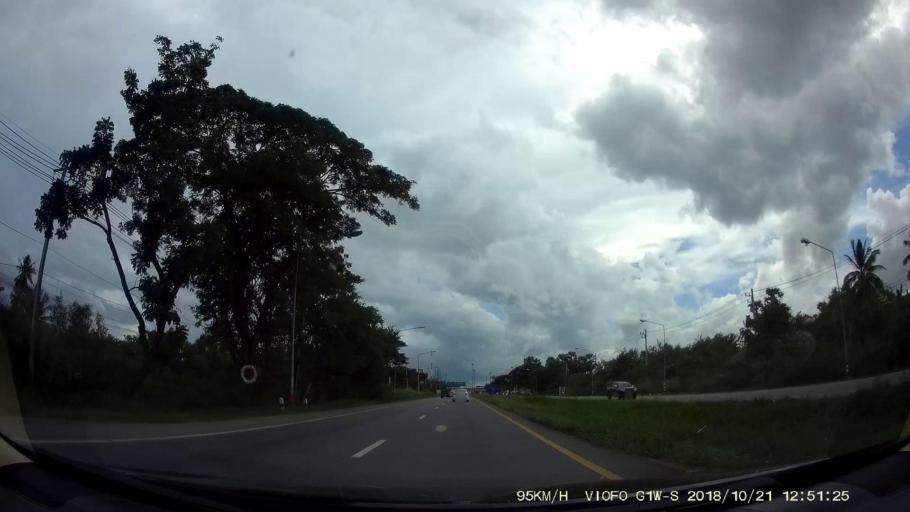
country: TH
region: Nakhon Ratchasima
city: Amphoe Sikhiu
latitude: 14.8687
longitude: 101.6959
